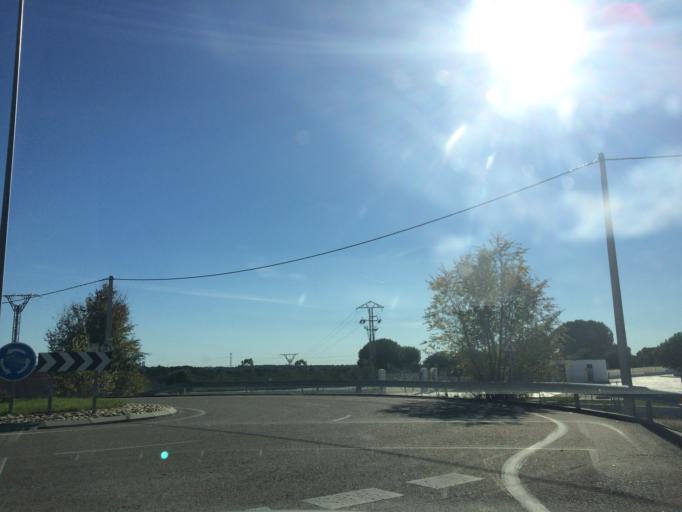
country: ES
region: Madrid
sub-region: Provincia de Madrid
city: Tres Cantos
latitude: 40.5971
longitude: -3.7187
